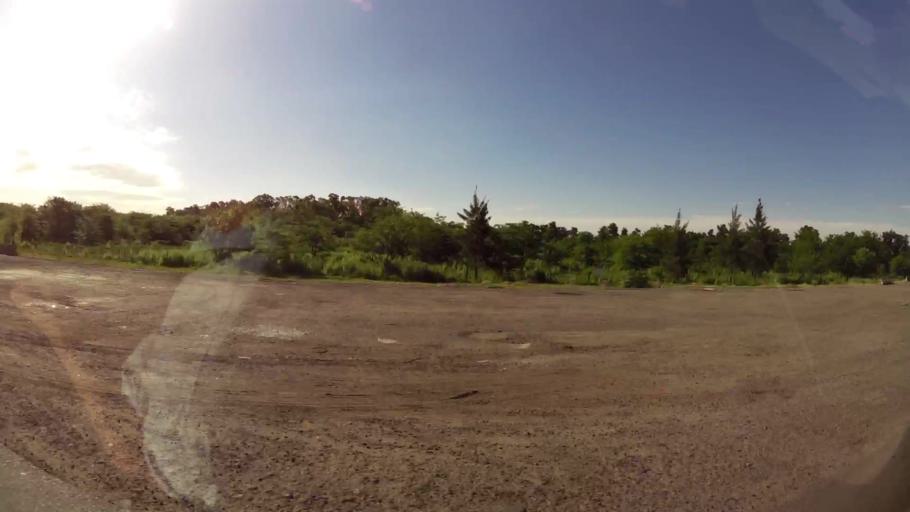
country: AR
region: Buenos Aires
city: Hurlingham
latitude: -34.5651
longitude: -58.6321
